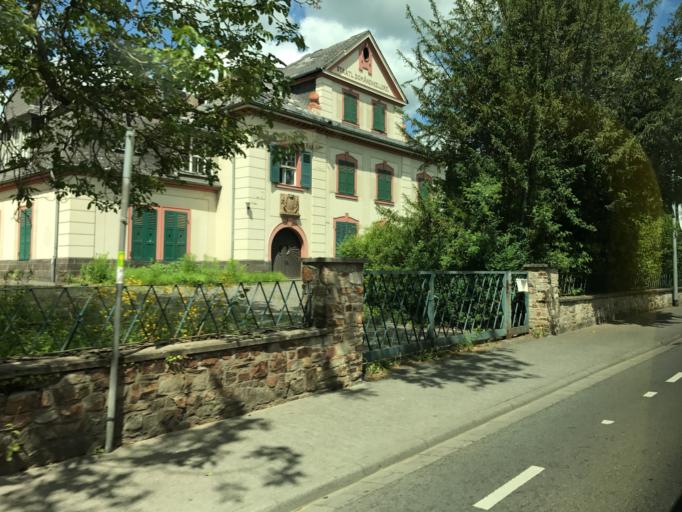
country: DE
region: Hesse
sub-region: Regierungsbezirk Darmstadt
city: Eltville
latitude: 50.0318
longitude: 8.1174
